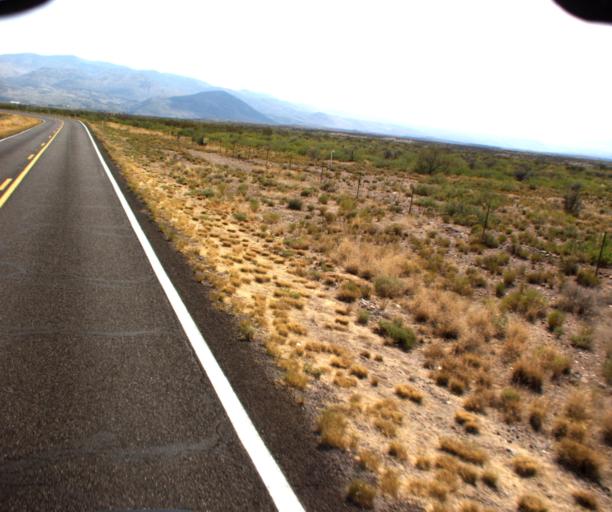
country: US
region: Arizona
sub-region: Greenlee County
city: Clifton
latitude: 32.9687
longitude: -109.2051
